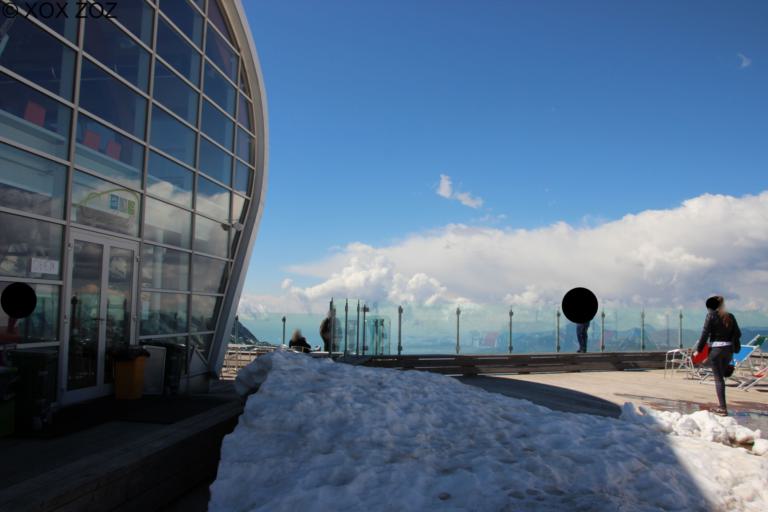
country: IT
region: Veneto
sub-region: Provincia di Verona
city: Malcesine
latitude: 45.7698
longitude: 10.8642
